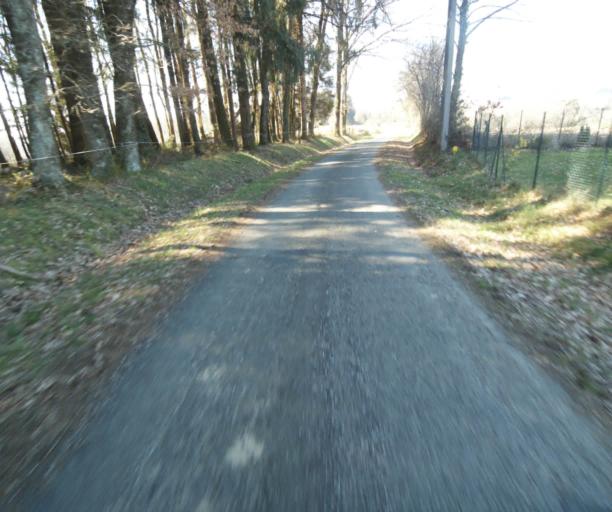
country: FR
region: Limousin
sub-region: Departement de la Correze
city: Saint-Mexant
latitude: 45.3058
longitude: 1.6026
